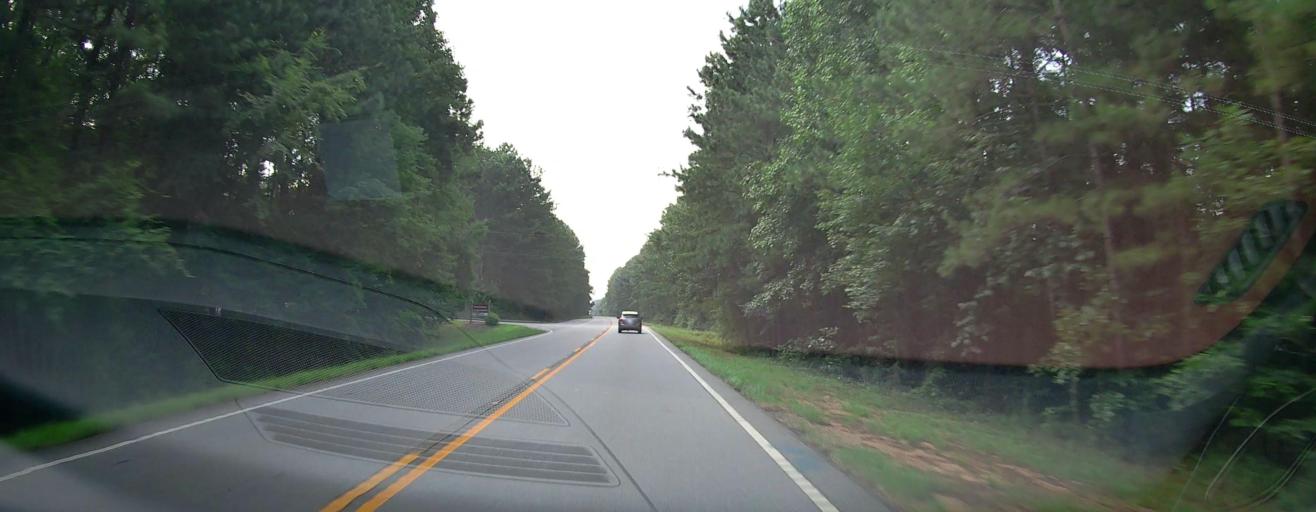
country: US
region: Georgia
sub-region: Monroe County
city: Forsyth
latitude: 33.0435
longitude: -83.7571
